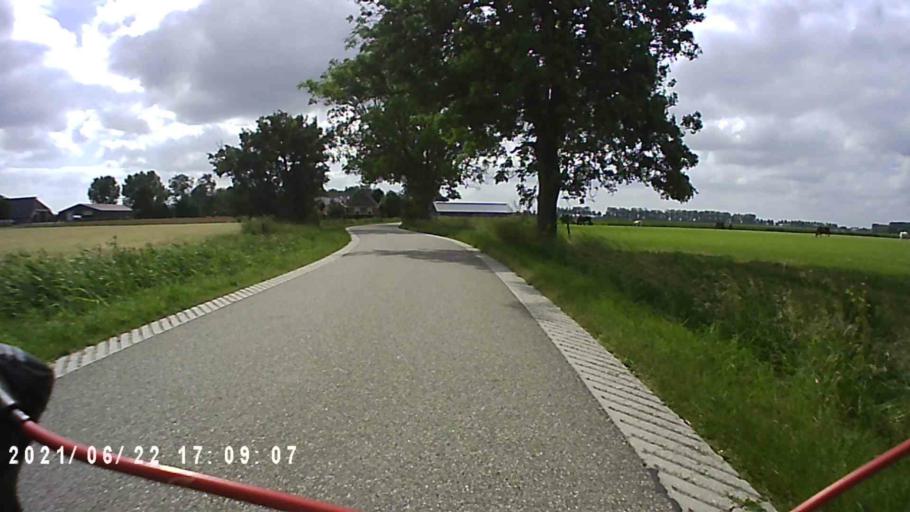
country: NL
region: Groningen
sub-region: Gemeente Bedum
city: Bedum
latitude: 53.2810
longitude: 6.6182
